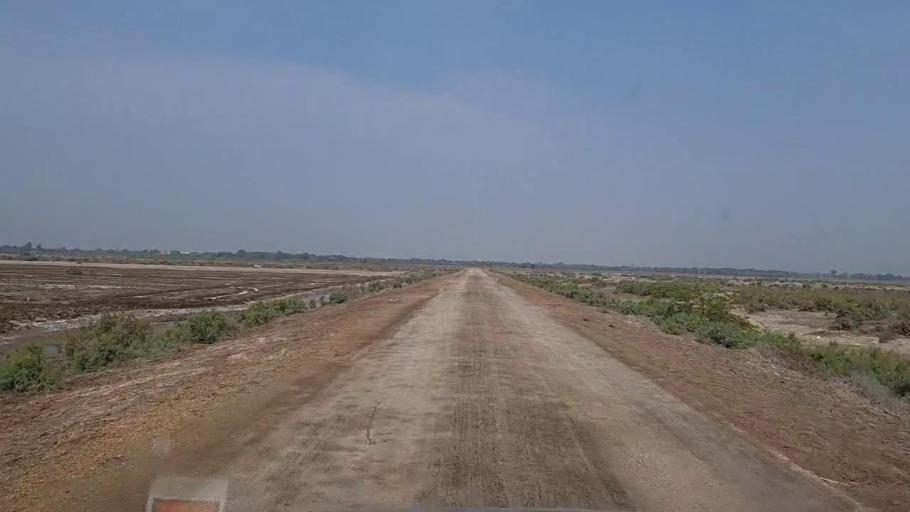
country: PK
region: Sindh
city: Mirwah Gorchani
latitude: 25.3307
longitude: 69.0615
